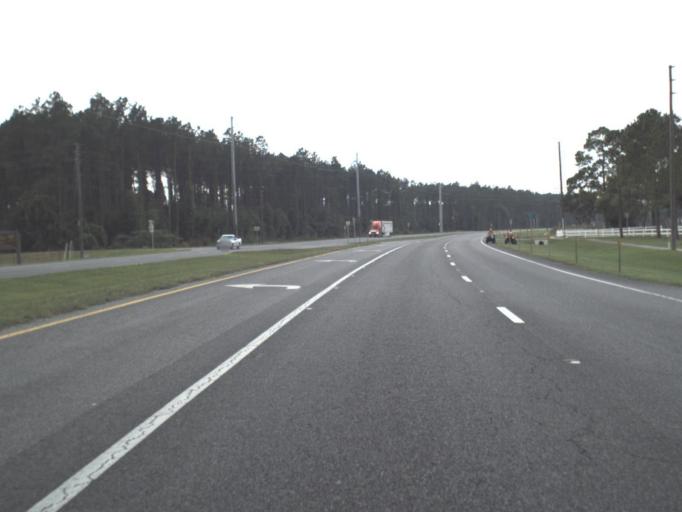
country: US
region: Florida
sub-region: Levy County
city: Chiefland
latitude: 29.4753
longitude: -82.8437
